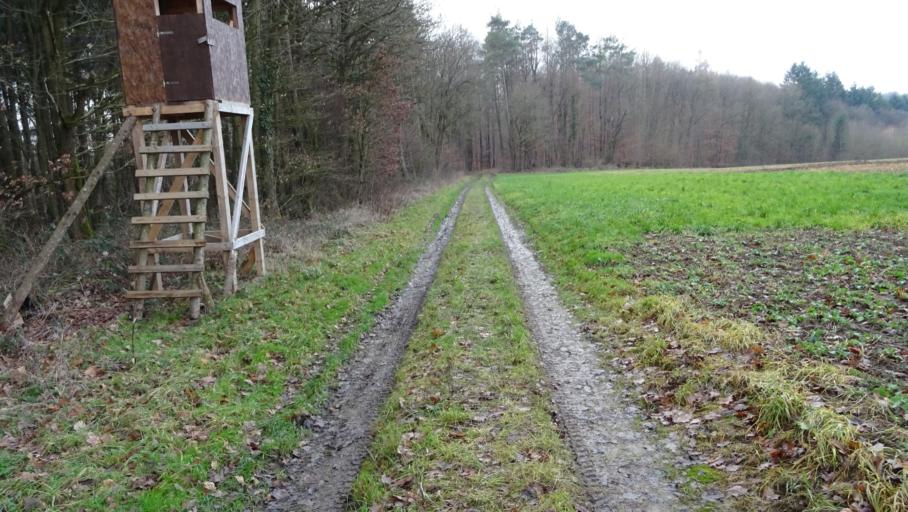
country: DE
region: Baden-Wuerttemberg
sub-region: Karlsruhe Region
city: Huffenhardt
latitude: 49.3081
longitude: 9.0579
